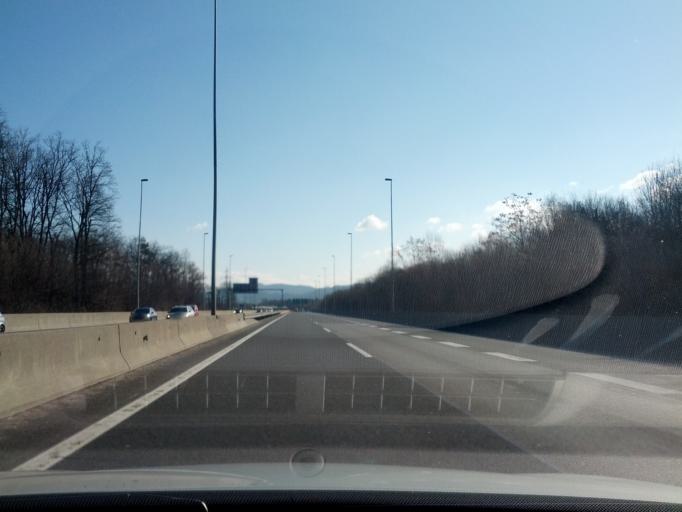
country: SI
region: Dol pri Ljubljani
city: Dol pri Ljubljani
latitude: 46.0674
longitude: 14.5625
